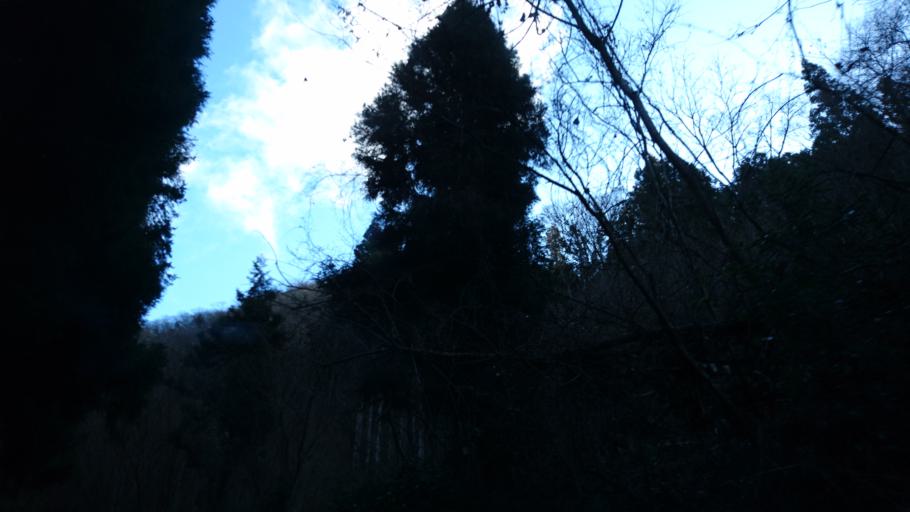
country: JP
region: Okayama
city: Takahashi
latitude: 34.8643
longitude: 133.5709
